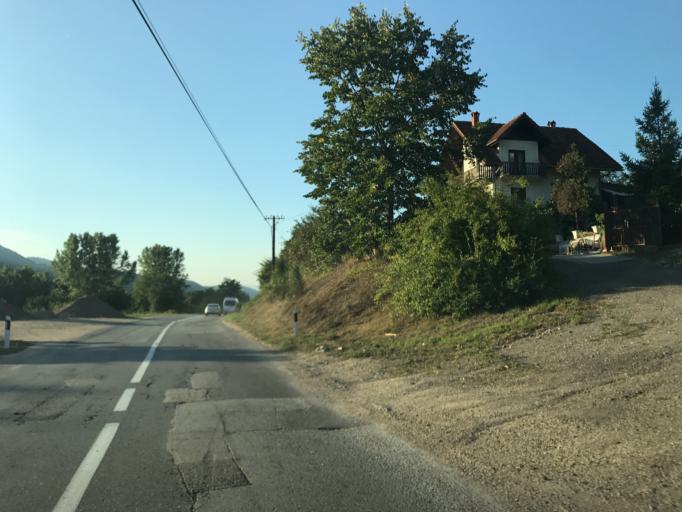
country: RO
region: Mehedinti
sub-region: Comuna Svinita
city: Svinita
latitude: 44.3566
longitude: 22.1809
